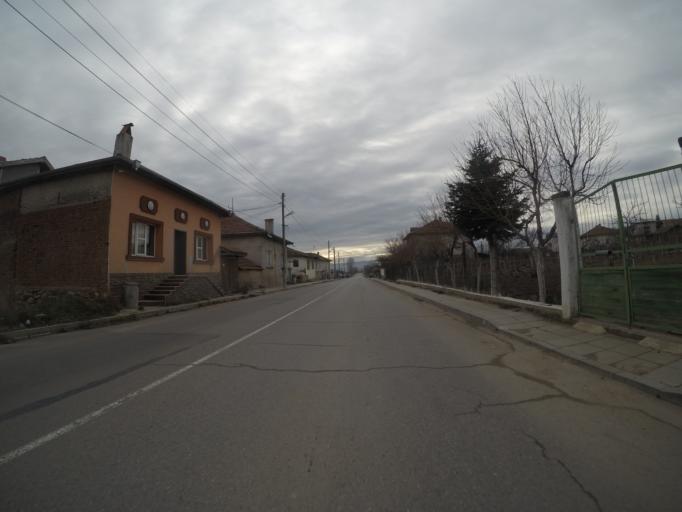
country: BG
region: Kyustendil
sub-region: Obshtina Rila
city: Rila
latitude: 42.1209
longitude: 23.1261
